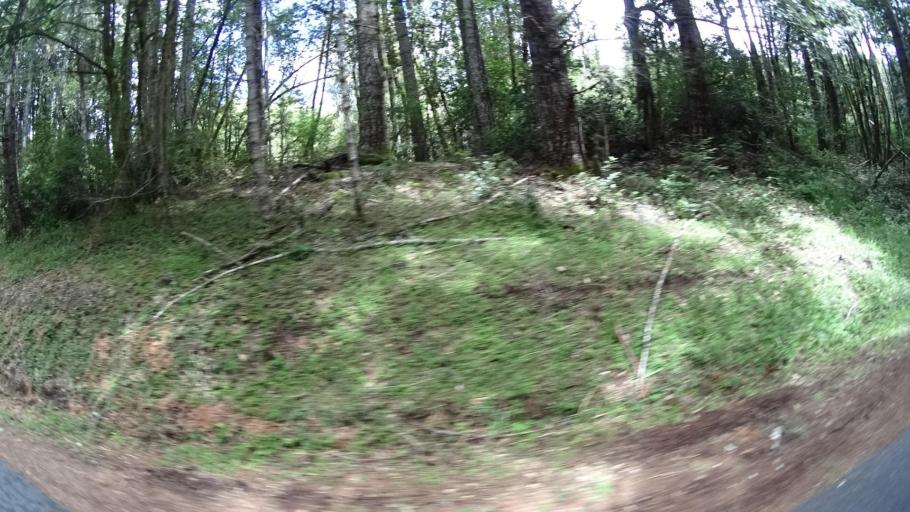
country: US
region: California
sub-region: Humboldt County
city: Blue Lake
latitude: 40.7968
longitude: -123.9822
